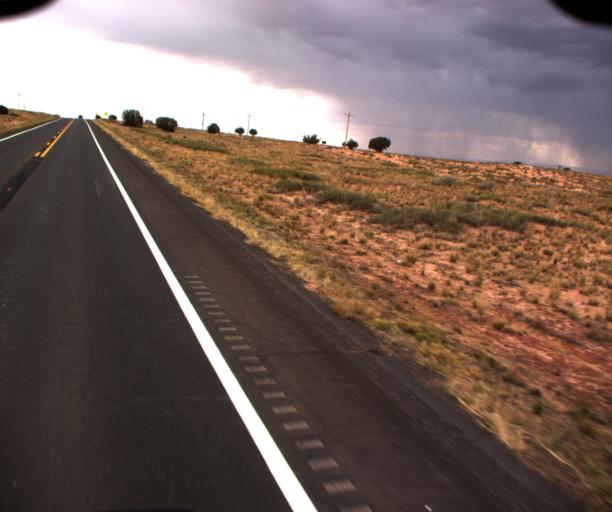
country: US
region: Arizona
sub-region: Coconino County
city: Tuba City
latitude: 36.2452
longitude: -111.0237
